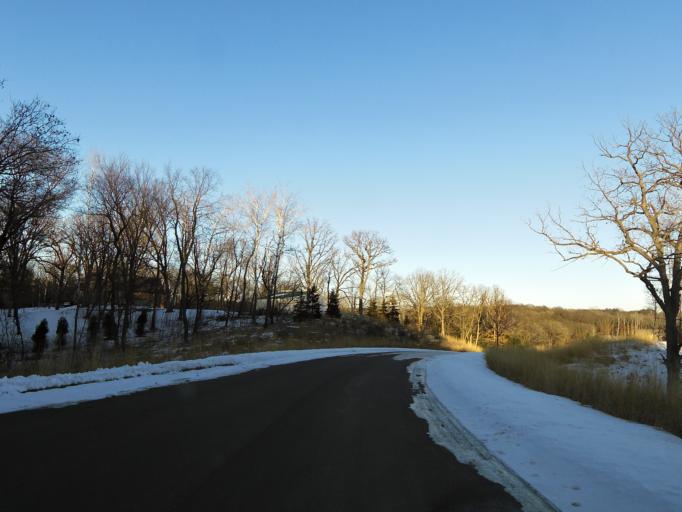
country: US
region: Minnesota
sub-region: Washington County
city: Lake Elmo
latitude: 44.9850
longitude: -92.8381
